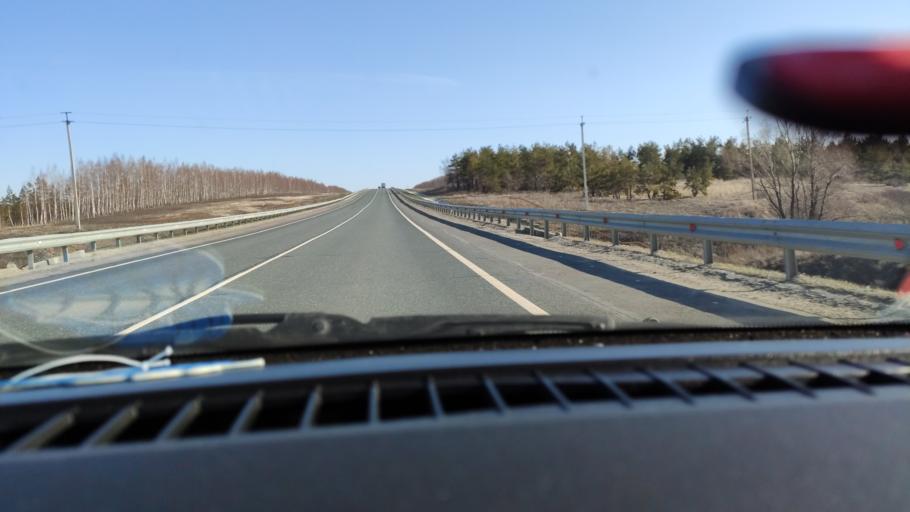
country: RU
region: Samara
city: Syzran'
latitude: 52.9015
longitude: 48.2968
